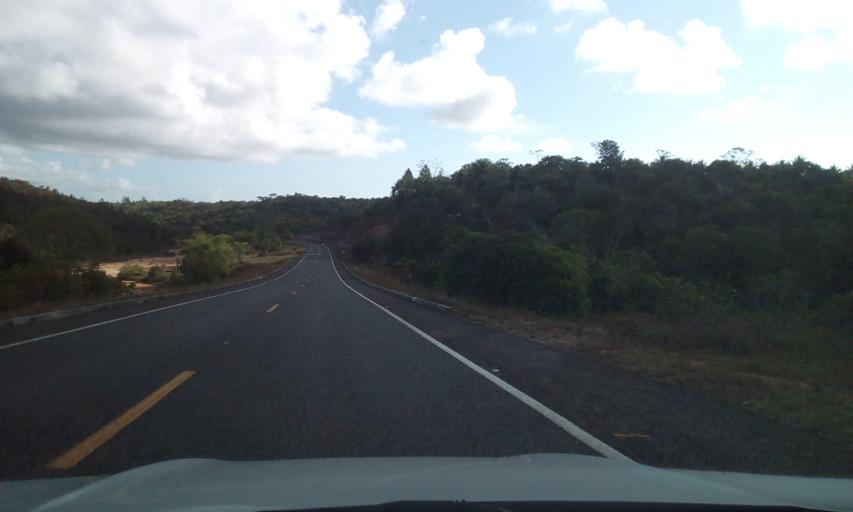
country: BR
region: Bahia
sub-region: Conde
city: Conde
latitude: -12.0761
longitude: -37.7547
